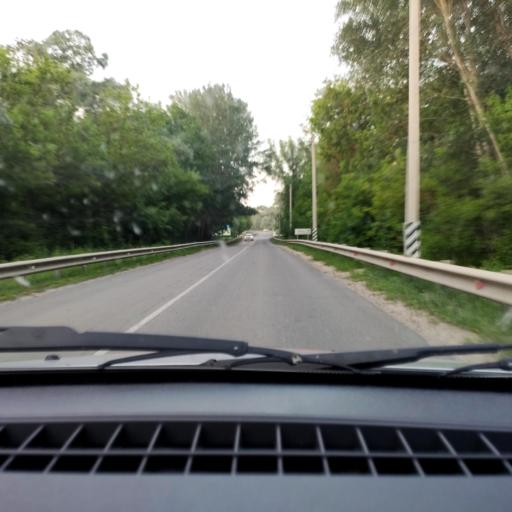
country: RU
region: Voronezj
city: Ramon'
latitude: 51.9491
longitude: 39.3791
